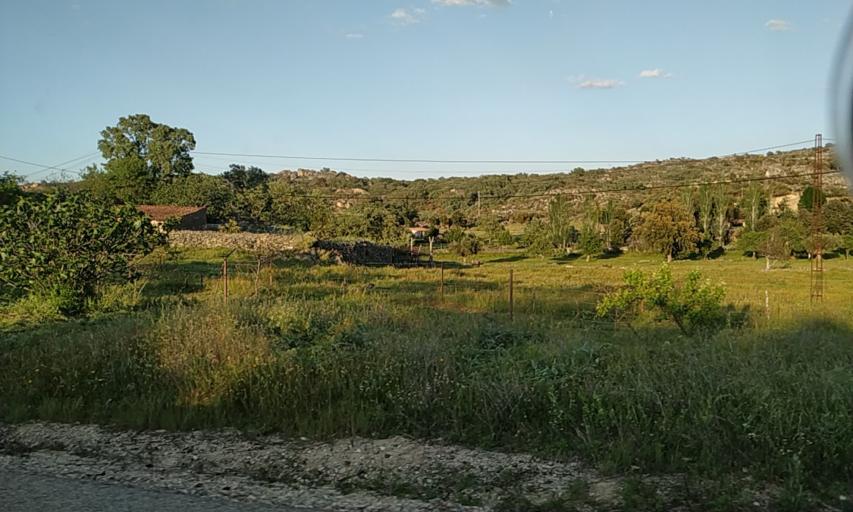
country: PT
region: Portalegre
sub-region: Portalegre
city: Sao Juliao
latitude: 39.3585
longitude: -7.2752
